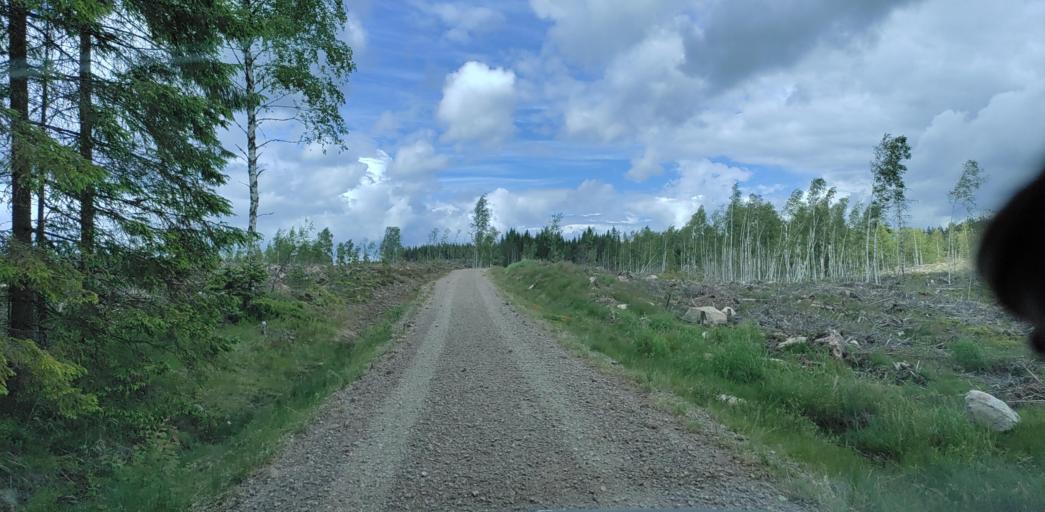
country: SE
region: Vaermland
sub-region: Munkfors Kommun
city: Munkfors
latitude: 59.9443
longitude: 13.4232
